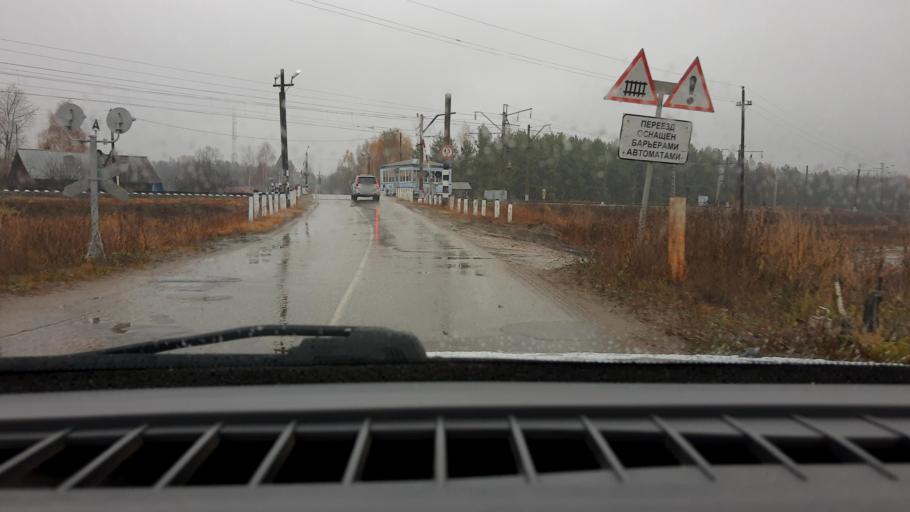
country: RU
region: Nizjnij Novgorod
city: Linda
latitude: 56.6845
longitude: 44.2020
